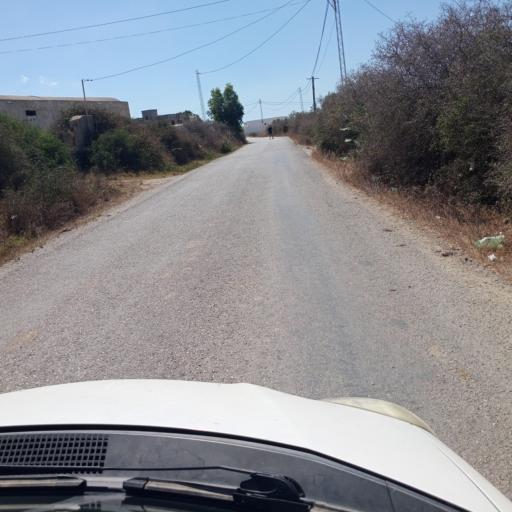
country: TN
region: Nabul
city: Qulaybiyah
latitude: 36.8648
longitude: 11.0339
